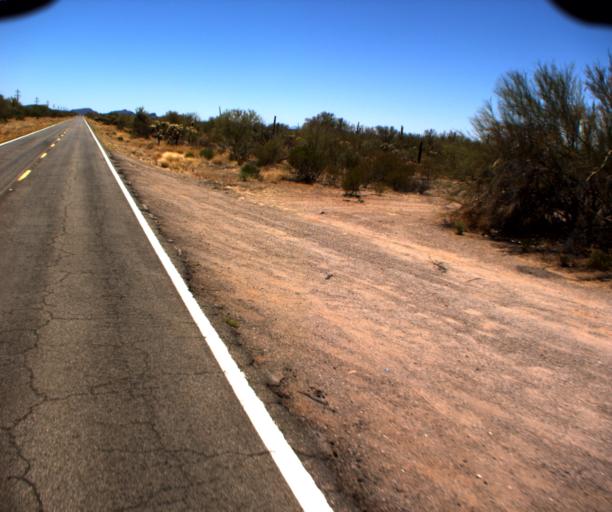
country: US
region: Arizona
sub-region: Pima County
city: Sells
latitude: 32.0417
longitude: -112.0187
